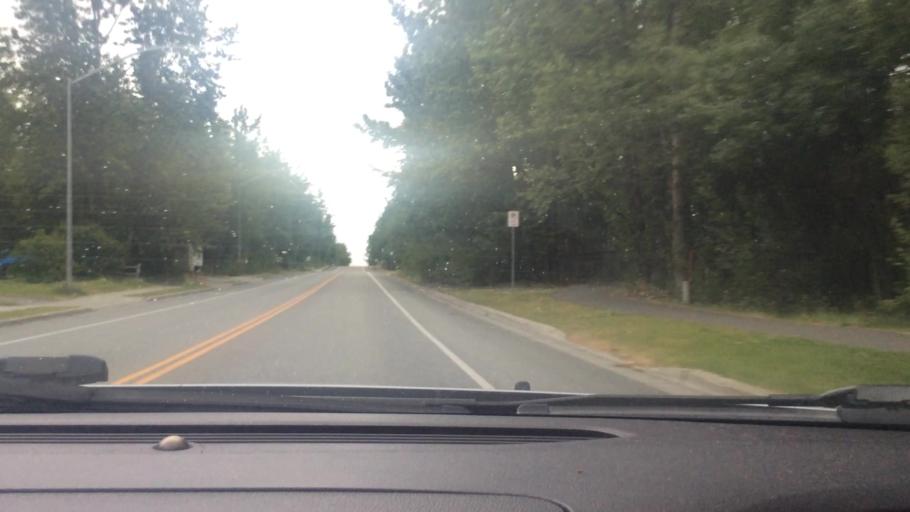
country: US
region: Alaska
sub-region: Anchorage Municipality
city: Anchorage
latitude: 61.1854
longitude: -149.7633
